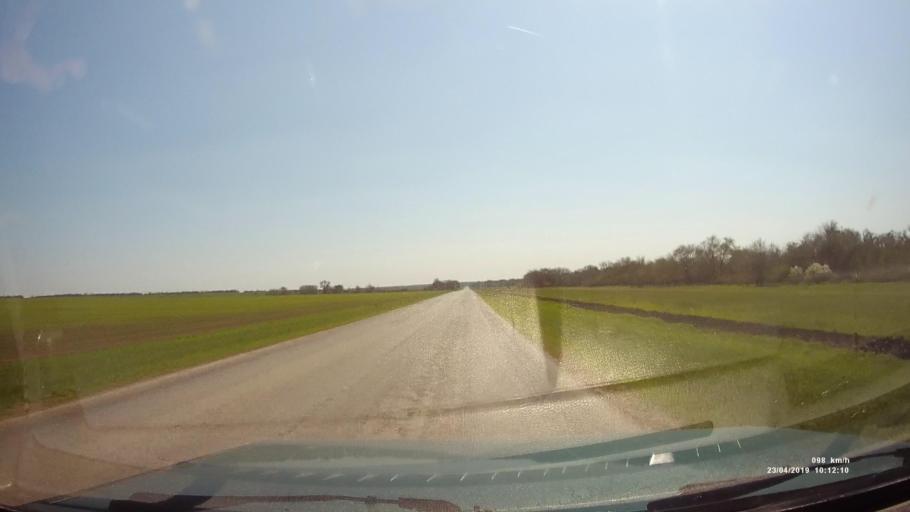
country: RU
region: Rostov
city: Sovetskoye
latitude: 46.6915
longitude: 42.3306
